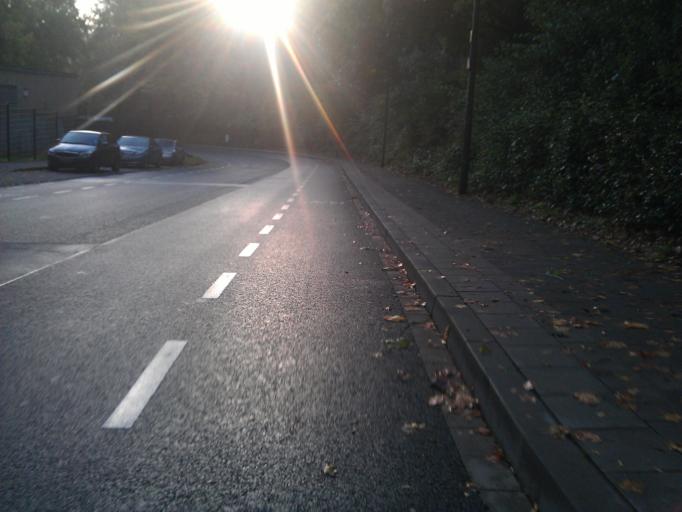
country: DE
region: North Rhine-Westphalia
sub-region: Regierungsbezirk Koln
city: Aachen
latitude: 50.7799
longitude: 6.0700
